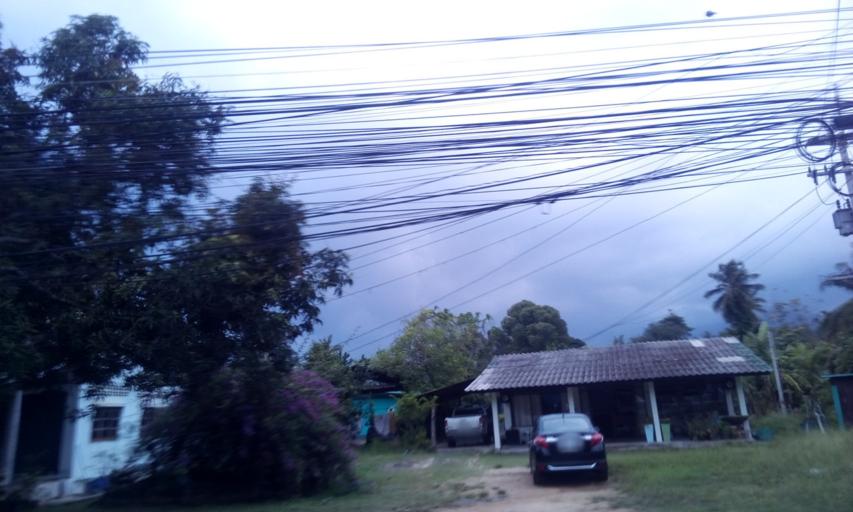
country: TH
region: Trat
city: Ko Chang Tai
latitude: 12.0384
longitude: 102.2940
